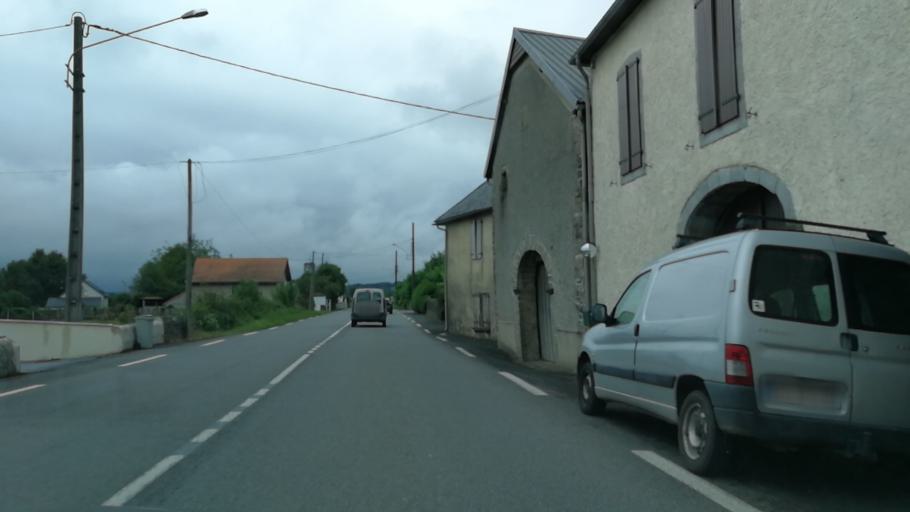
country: FR
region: Aquitaine
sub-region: Departement des Pyrenees-Atlantiques
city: Oloron-Sainte-Marie
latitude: 43.1462
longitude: -0.6010
